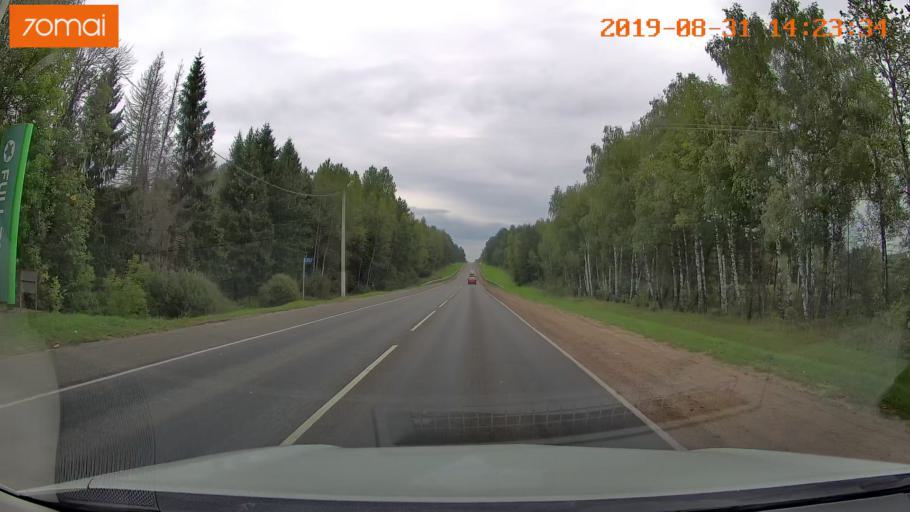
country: RU
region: Smolensk
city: Yekimovichi
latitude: 54.0973
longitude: 33.2365
